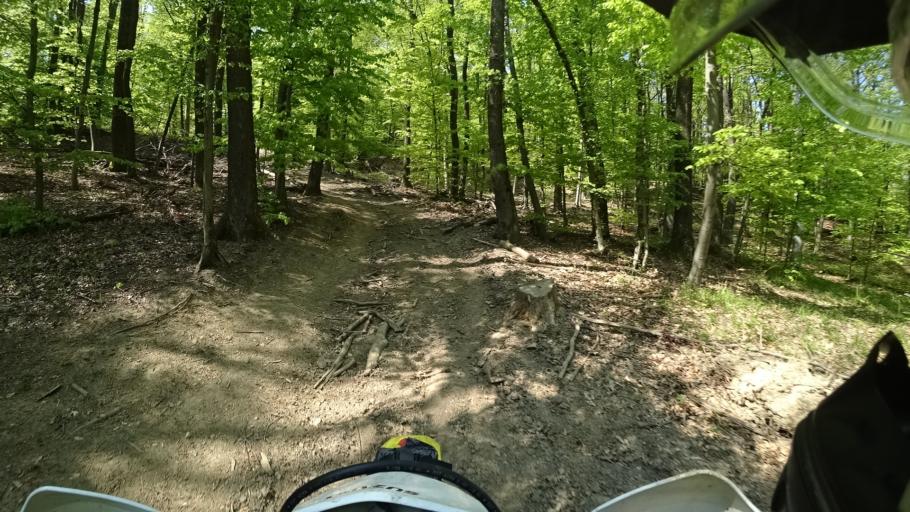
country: HR
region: Zagrebacka
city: Jablanovec
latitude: 45.8592
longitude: 15.9057
